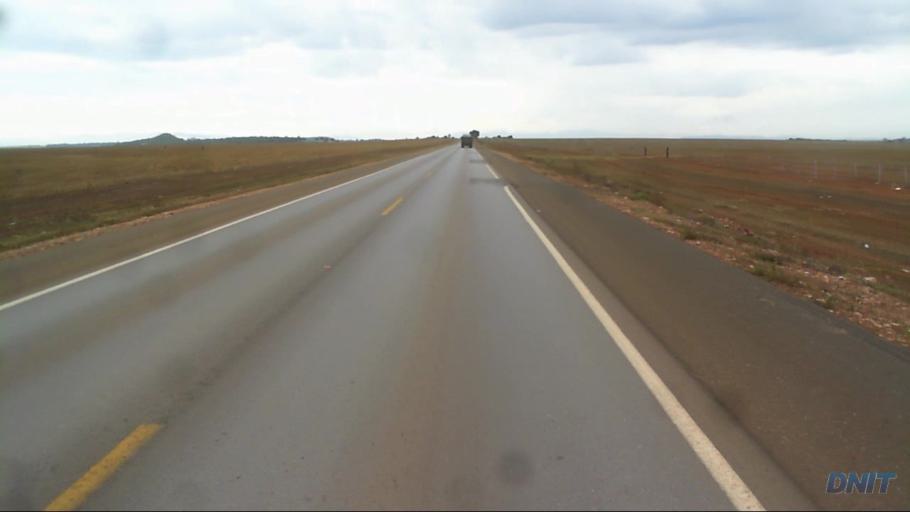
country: BR
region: Goias
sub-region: Uruacu
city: Uruacu
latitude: -14.6458
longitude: -49.1676
